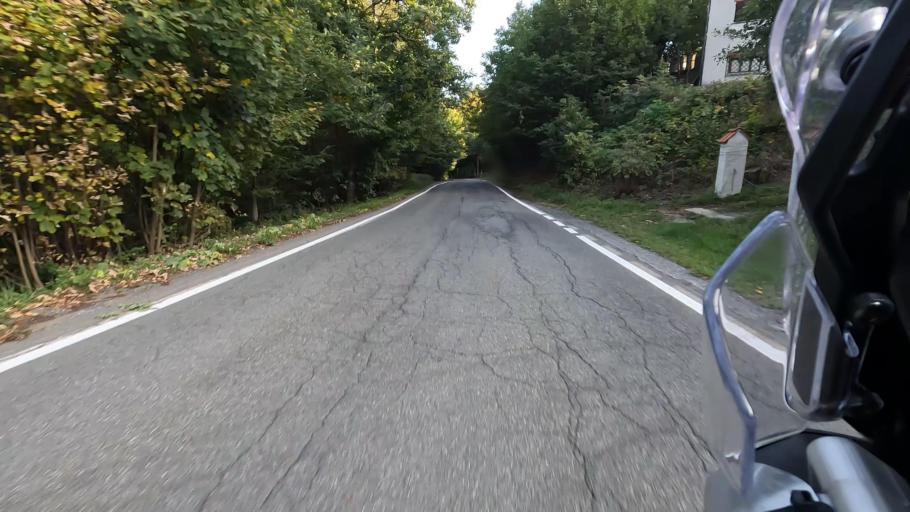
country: IT
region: Liguria
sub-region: Provincia di Savona
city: Urbe
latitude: 44.4614
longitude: 8.5507
